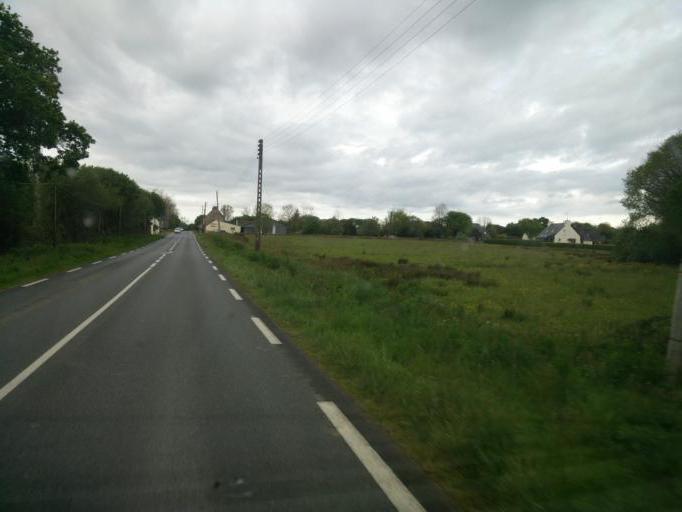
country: FR
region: Brittany
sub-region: Departement des Cotes-d'Armor
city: Ploumilliau
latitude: 48.7080
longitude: -3.5035
